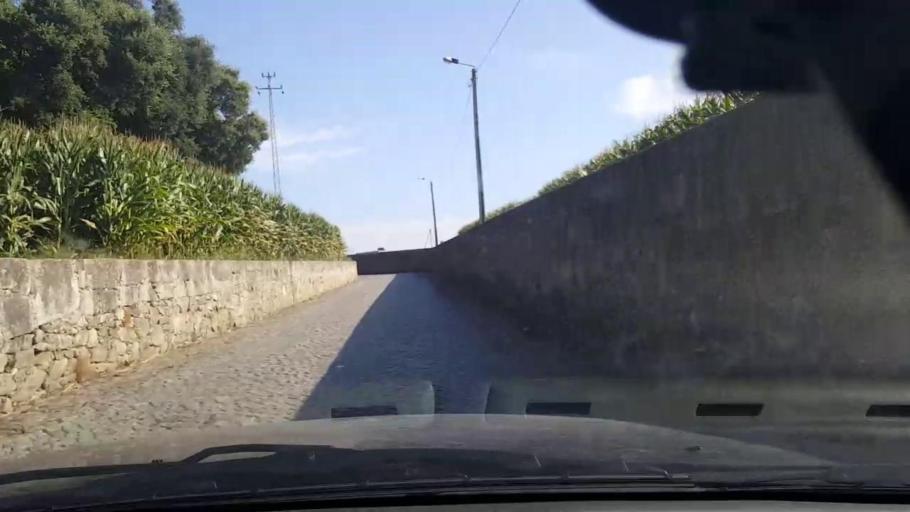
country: PT
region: Porto
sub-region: Maia
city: Gemunde
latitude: 41.2749
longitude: -8.6690
